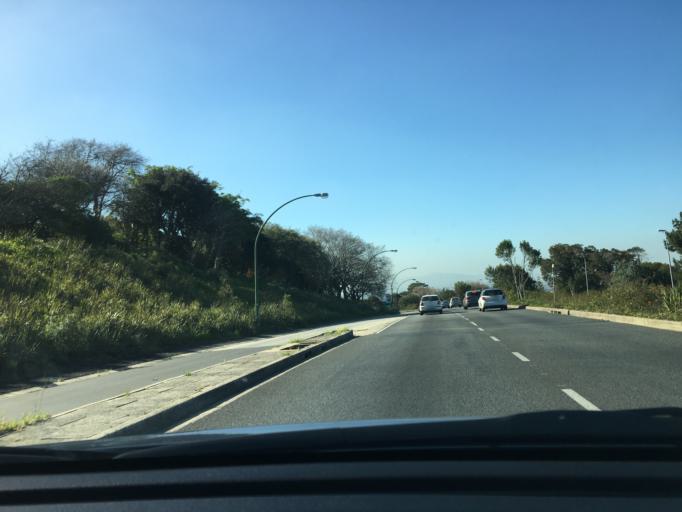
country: ZA
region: Western Cape
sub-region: City of Cape Town
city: Newlands
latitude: -33.9955
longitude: 18.4540
